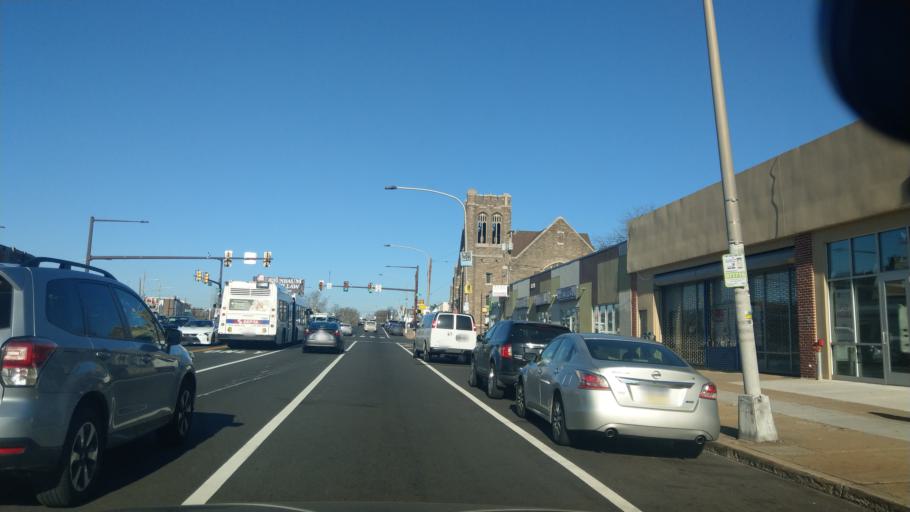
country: US
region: Pennsylvania
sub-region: Montgomery County
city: Wyncote
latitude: 40.0407
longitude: -75.1443
